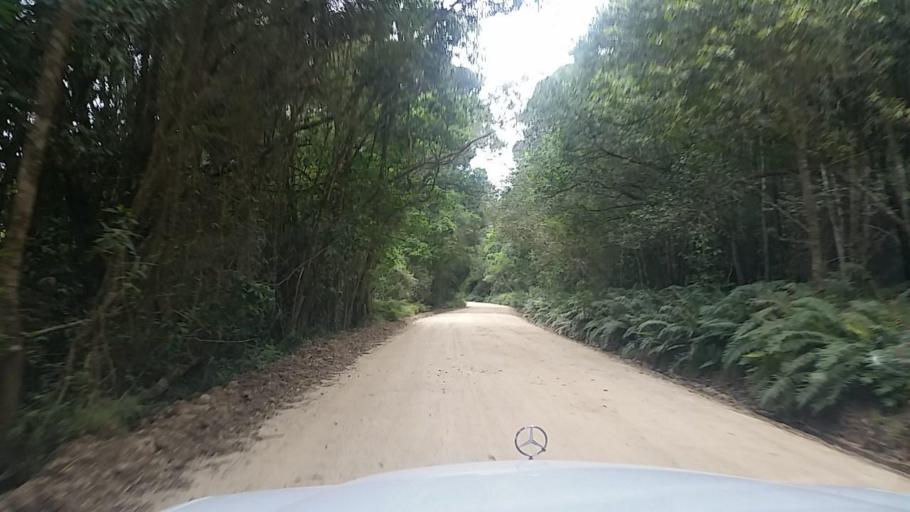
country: ZA
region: Western Cape
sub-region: Eden District Municipality
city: Knysna
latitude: -33.9423
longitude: 23.1605
